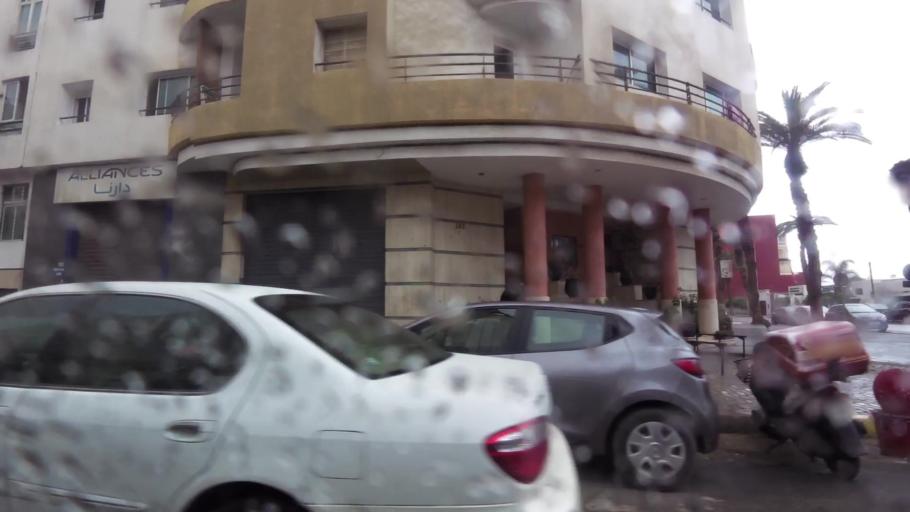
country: MA
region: Grand Casablanca
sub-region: Casablanca
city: Casablanca
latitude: 33.6025
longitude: -7.6453
